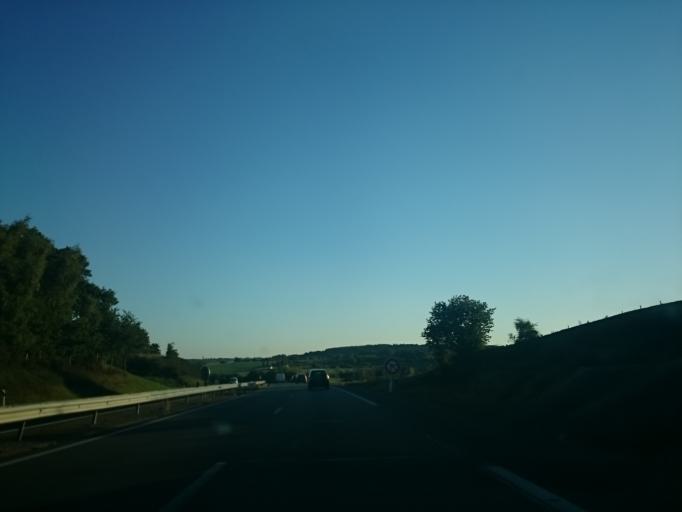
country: FR
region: Brittany
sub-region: Departement d'Ille-et-Vilaine
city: Pance
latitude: 47.8890
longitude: -1.6902
